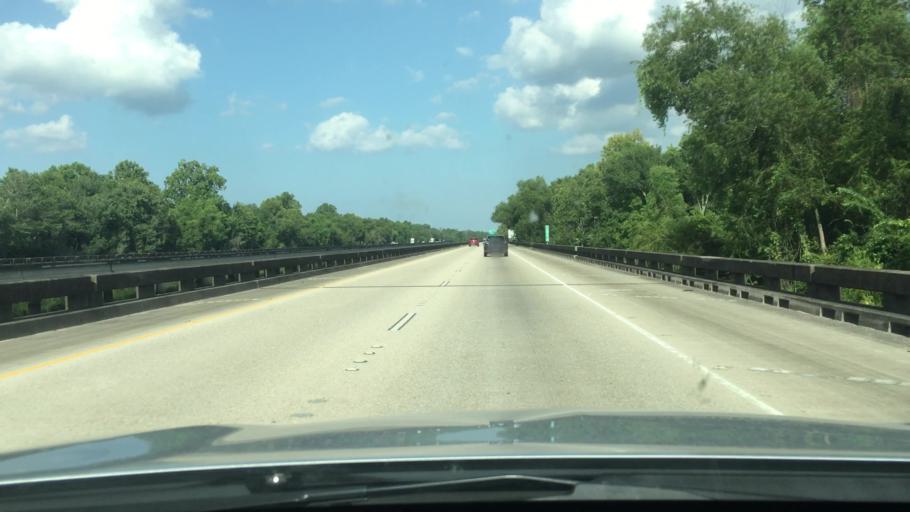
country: US
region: Louisiana
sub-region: Saint John the Baptist Parish
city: Montegut
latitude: 30.1085
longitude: -90.5200
